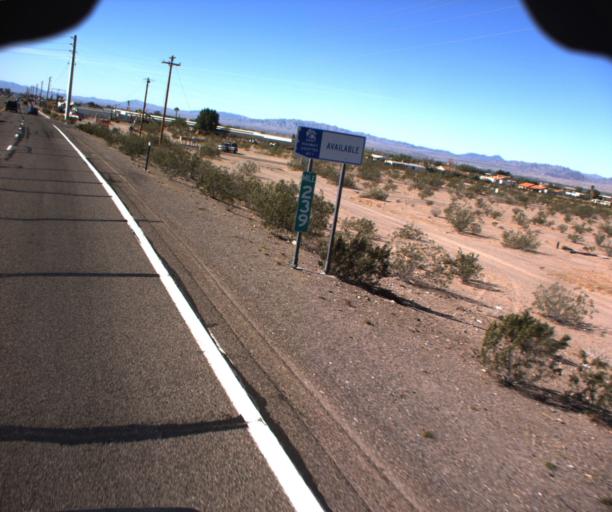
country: US
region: Arizona
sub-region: Mohave County
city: Mohave Valley
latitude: 35.0342
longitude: -114.5980
